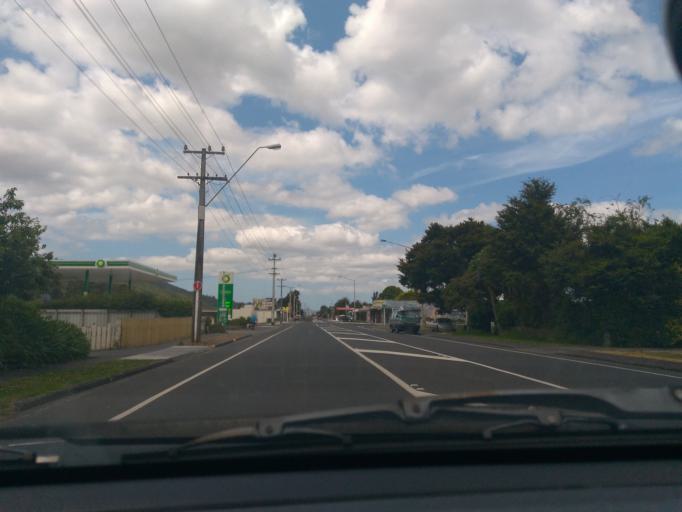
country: NZ
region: Northland
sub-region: Far North District
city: Moerewa
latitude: -35.3883
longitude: 174.0126
